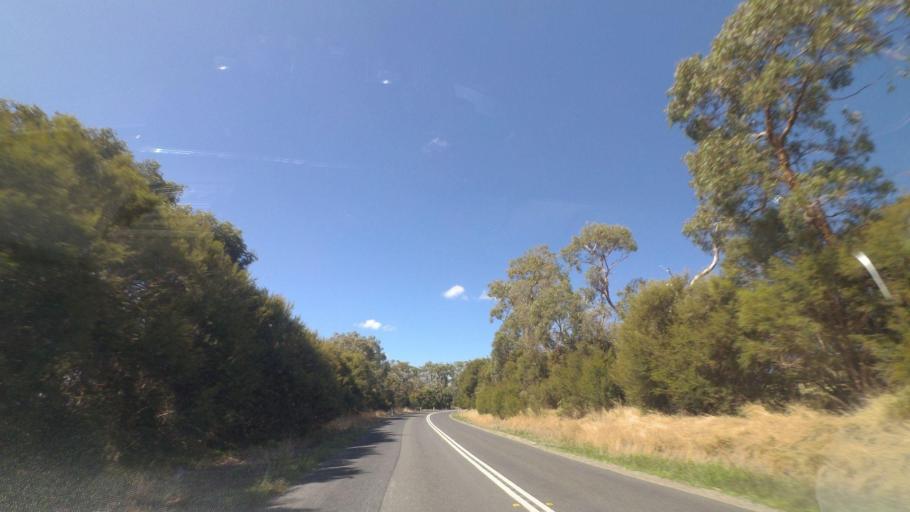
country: AU
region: Victoria
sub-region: Cardinia
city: Bunyip
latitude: -38.2488
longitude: 145.6813
